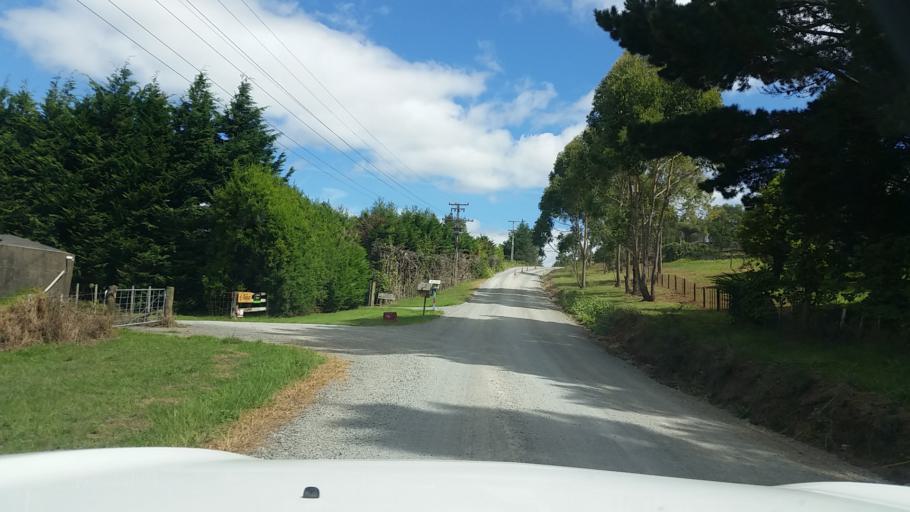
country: NZ
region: Northland
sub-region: Whangarei
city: Whangarei
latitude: -35.6632
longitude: 174.3494
